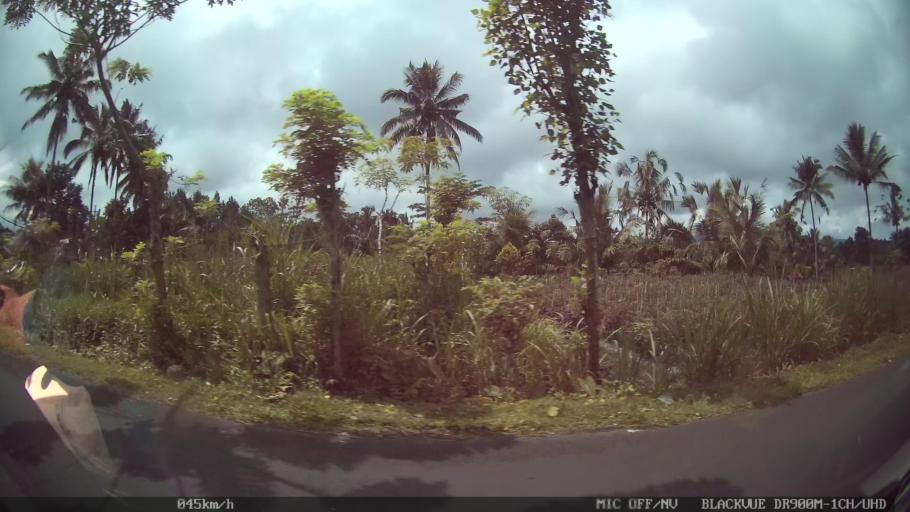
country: ID
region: Bali
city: Banjar Geriana Kangin
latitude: -8.4200
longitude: 115.4364
